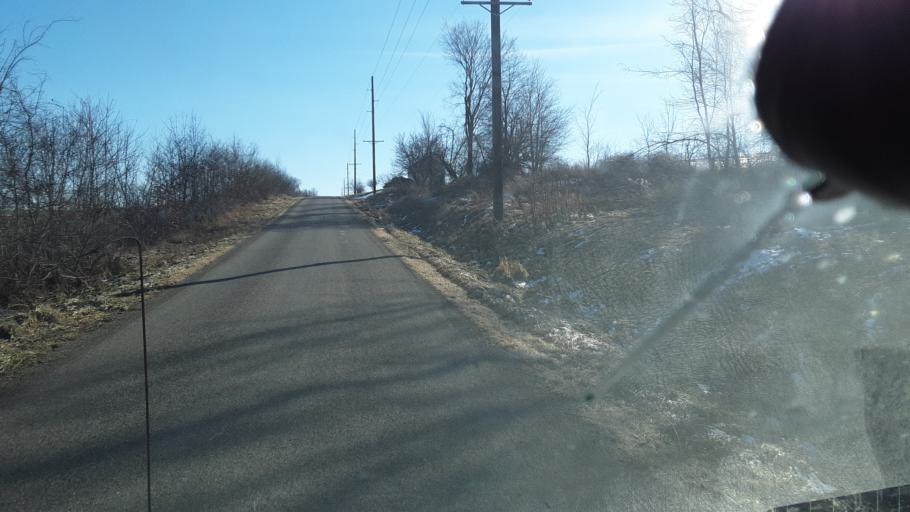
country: US
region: Ohio
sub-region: Ashland County
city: Loudonville
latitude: 40.7074
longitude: -82.2125
